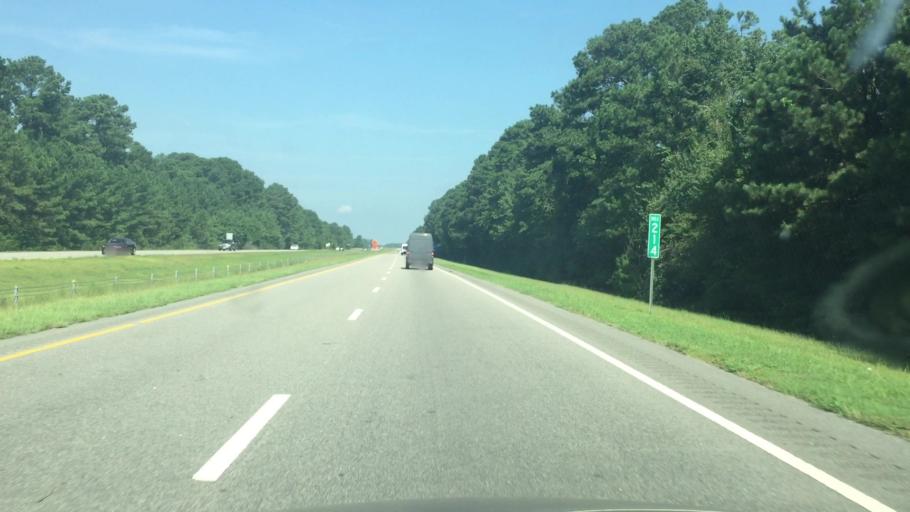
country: US
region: North Carolina
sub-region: Robeson County
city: Lumberton
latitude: 34.5731
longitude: -79.0356
